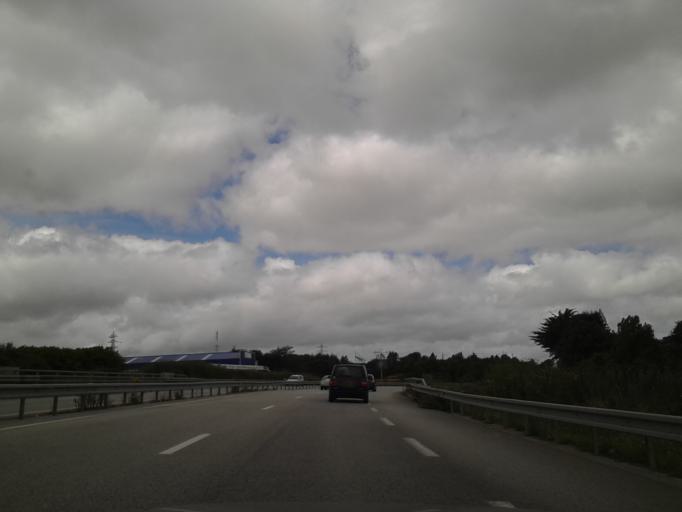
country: FR
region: Lower Normandy
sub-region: Departement de la Manche
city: La Glacerie
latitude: 49.5873
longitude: -1.5964
